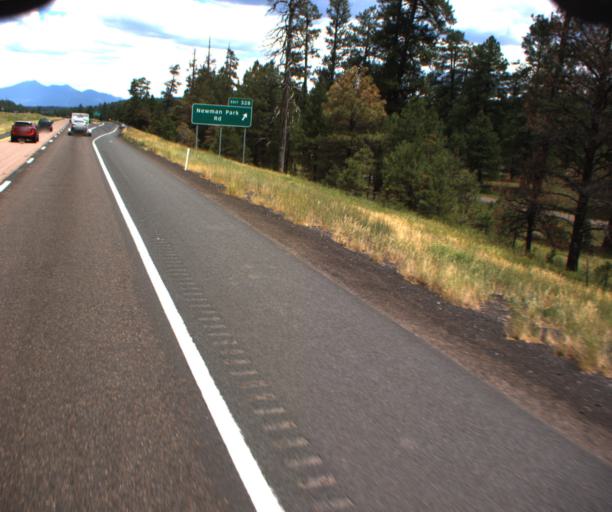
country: US
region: Arizona
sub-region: Coconino County
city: Mountainaire
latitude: 35.0136
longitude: -111.6848
